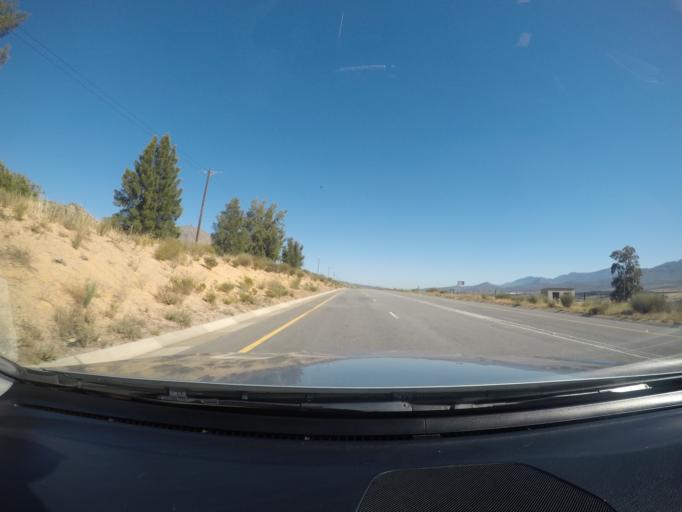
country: ZA
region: Western Cape
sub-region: West Coast District Municipality
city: Clanwilliam
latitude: -32.5405
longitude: 18.9775
